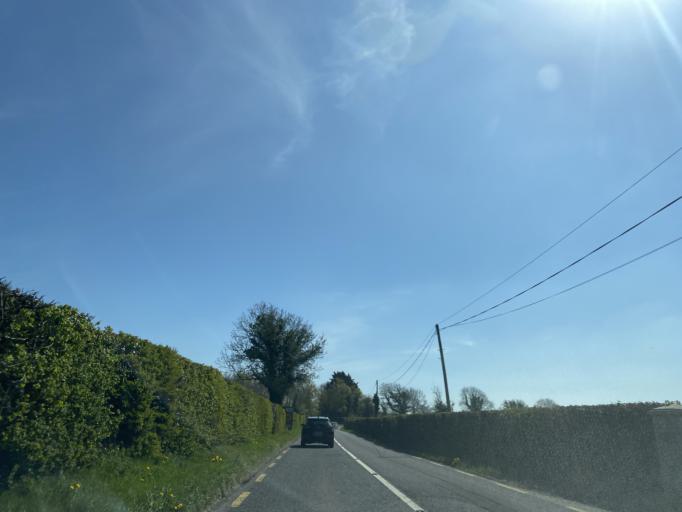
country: IE
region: Leinster
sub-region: Kildare
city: Kill
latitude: 53.2743
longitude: -6.5917
